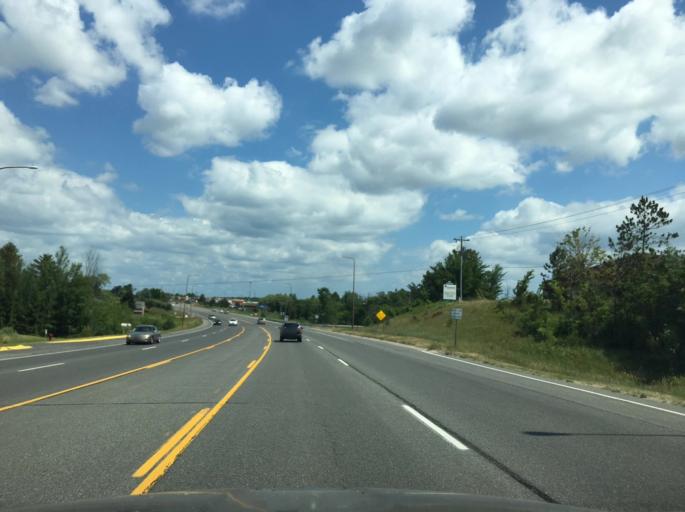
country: US
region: Michigan
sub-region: Grand Traverse County
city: Traverse City
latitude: 44.7167
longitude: -85.6469
